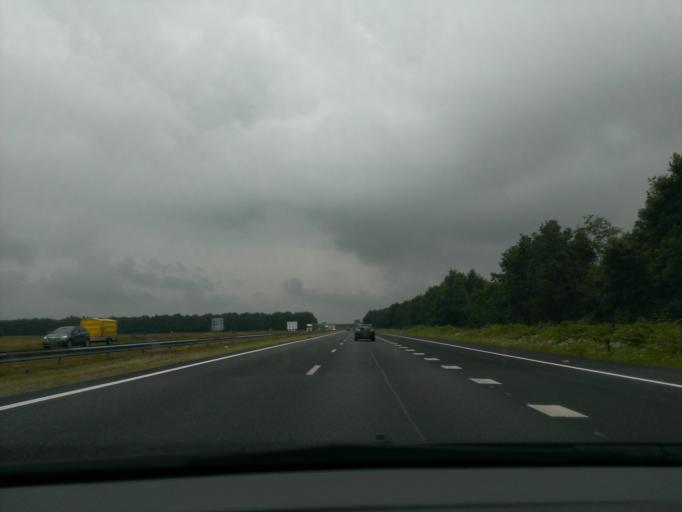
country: NL
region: Drenthe
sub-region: Gemeente Assen
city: Assen
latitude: 52.9487
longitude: 6.5411
